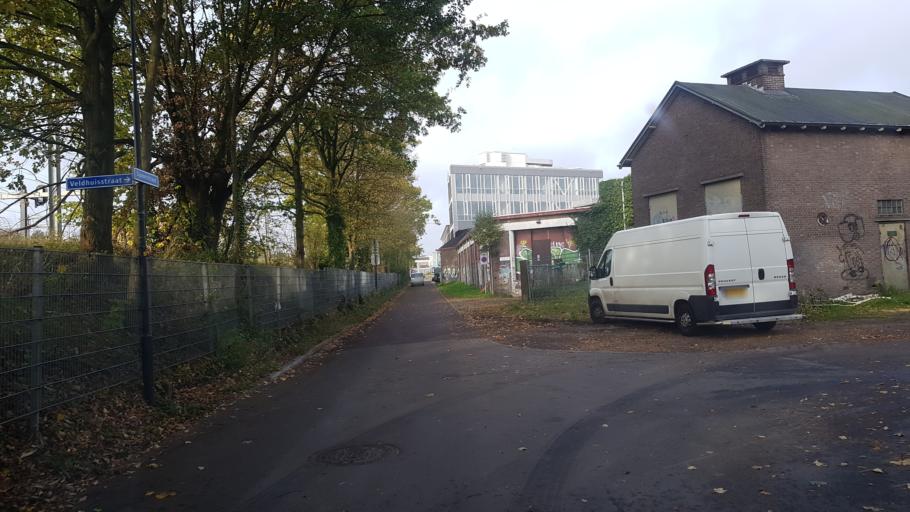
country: NL
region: Gelderland
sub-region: Gemeente Apeldoorn
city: Apeldoorn
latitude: 52.2094
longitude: 5.9753
